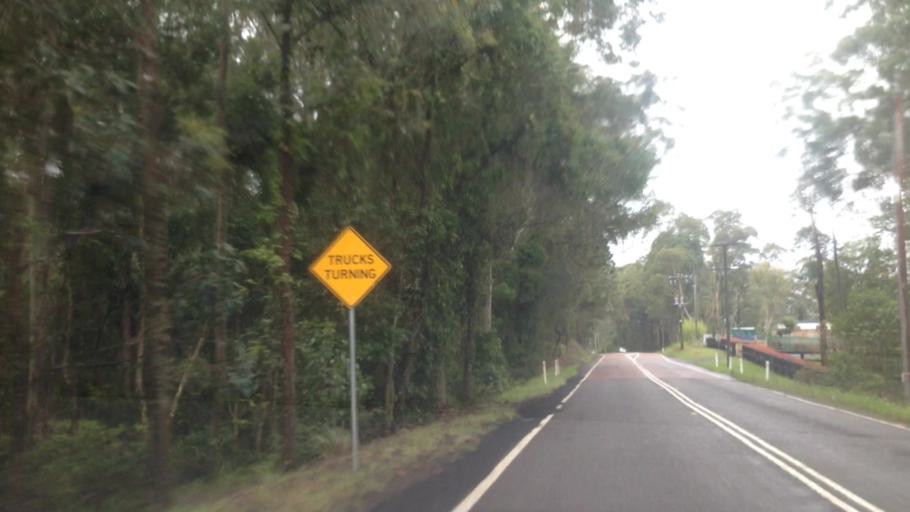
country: AU
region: New South Wales
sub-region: Wyong Shire
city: Little Jilliby
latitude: -33.2524
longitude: 151.3974
